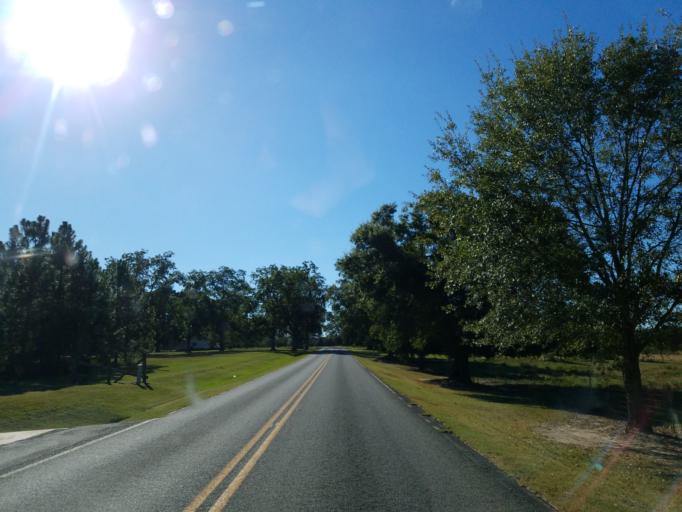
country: US
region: Georgia
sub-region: Dooly County
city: Unadilla
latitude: 32.2526
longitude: -83.7856
